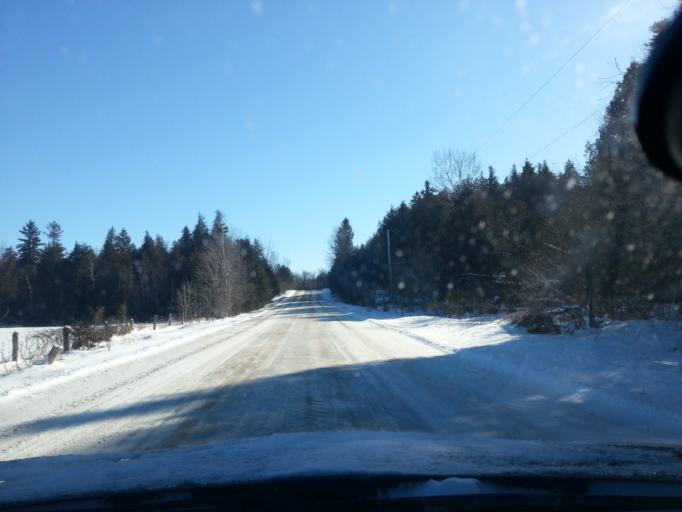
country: CA
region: Ontario
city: Arnprior
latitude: 45.2500
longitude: -76.3109
